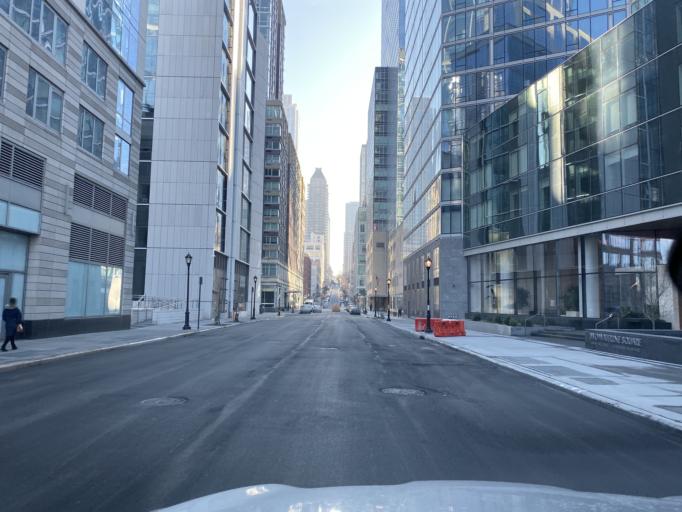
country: US
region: New Jersey
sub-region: Hudson County
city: Guttenberg
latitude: 40.7737
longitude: -73.9915
